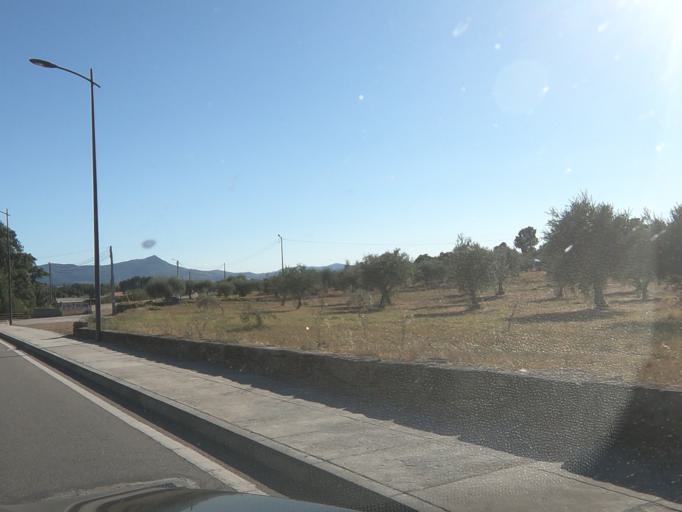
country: PT
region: Vila Real
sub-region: Valpacos
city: Valpacos
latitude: 41.5891
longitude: -7.3075
